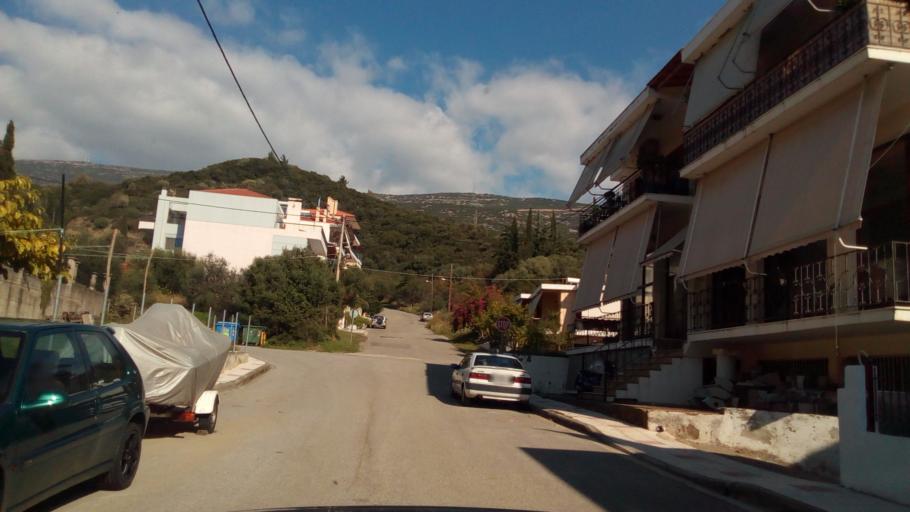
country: GR
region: West Greece
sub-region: Nomos Aitolias kai Akarnanias
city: Nafpaktos
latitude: 38.3930
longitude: 21.8158
